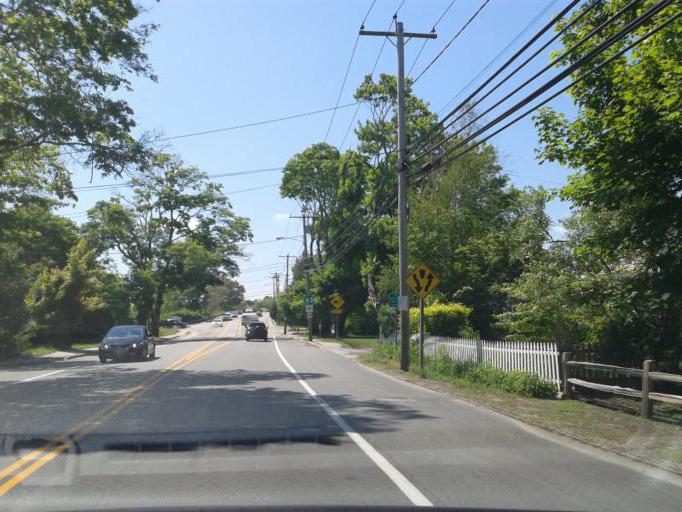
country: US
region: Rhode Island
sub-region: Washington County
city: Kingston
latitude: 41.4839
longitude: -71.5565
